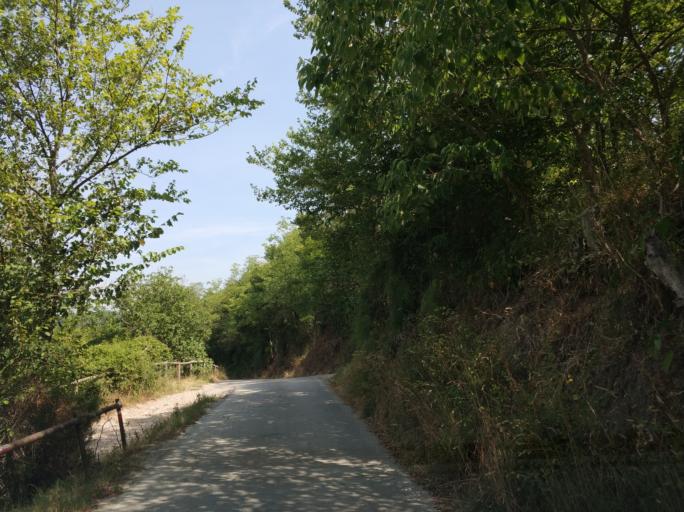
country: IT
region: Veneto
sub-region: Provincia di Padova
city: Arqua Petrarca
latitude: 45.2796
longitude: 11.7059
